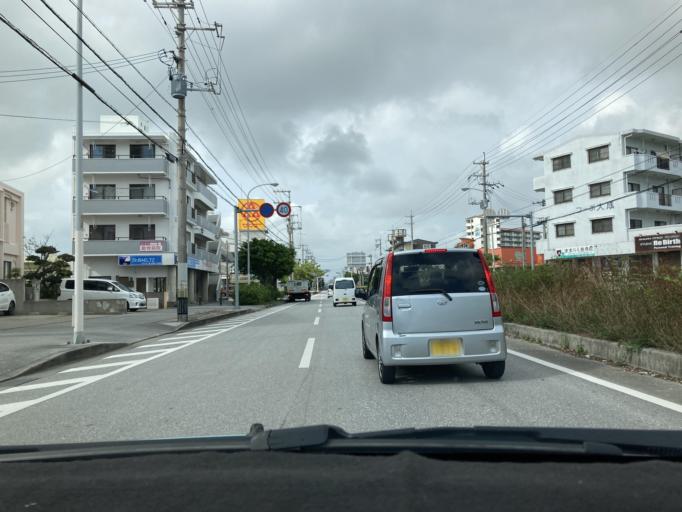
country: JP
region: Okinawa
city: Itoman
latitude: 26.1520
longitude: 127.6720
